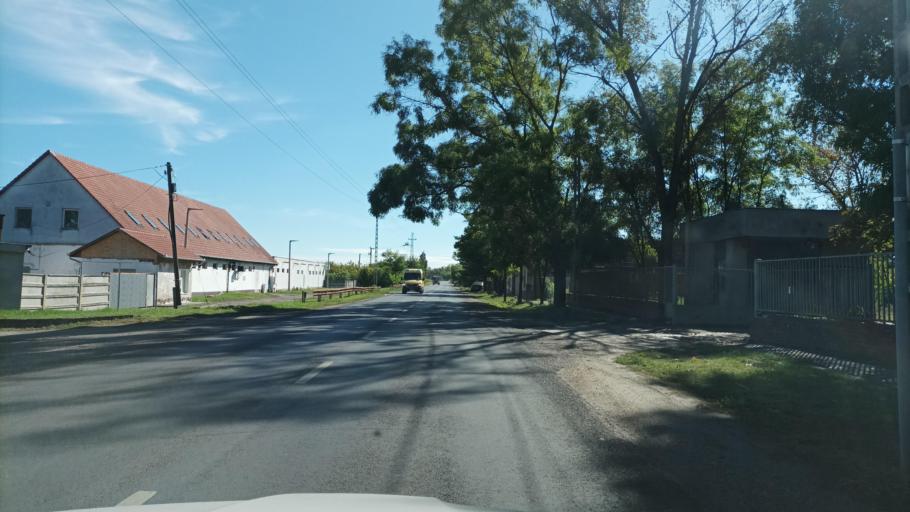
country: HU
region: Pest
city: Cegled
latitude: 47.1712
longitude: 19.8199
